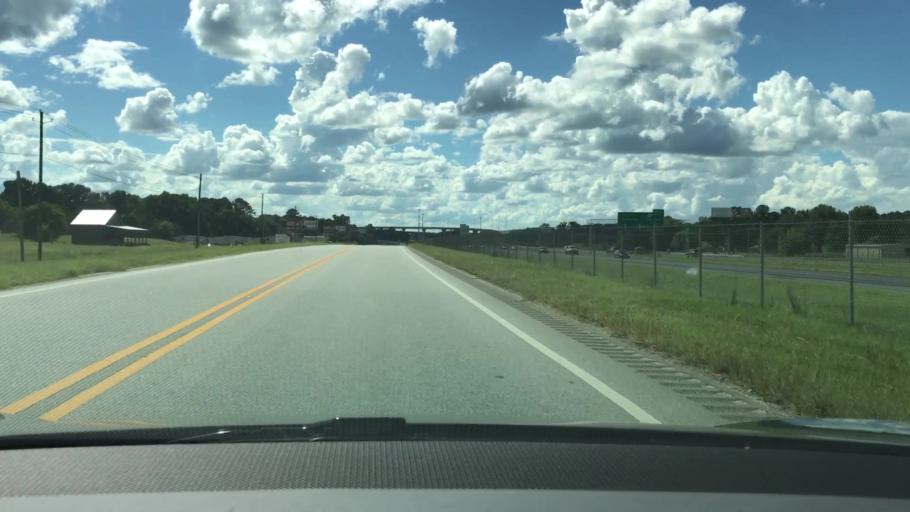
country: US
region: Alabama
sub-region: Montgomery County
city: Pike Road
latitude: 32.3675
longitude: -86.0604
